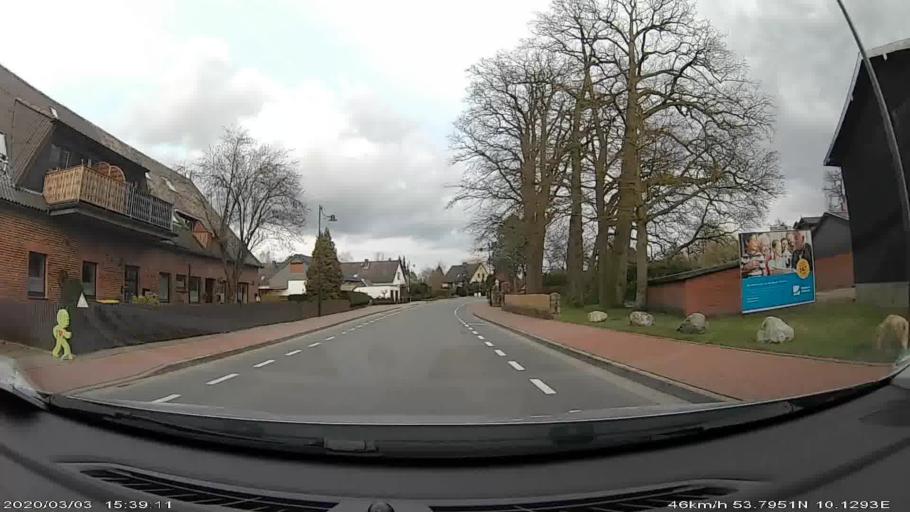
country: DE
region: Schleswig-Holstein
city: Nahe
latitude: 53.7949
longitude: 10.1284
